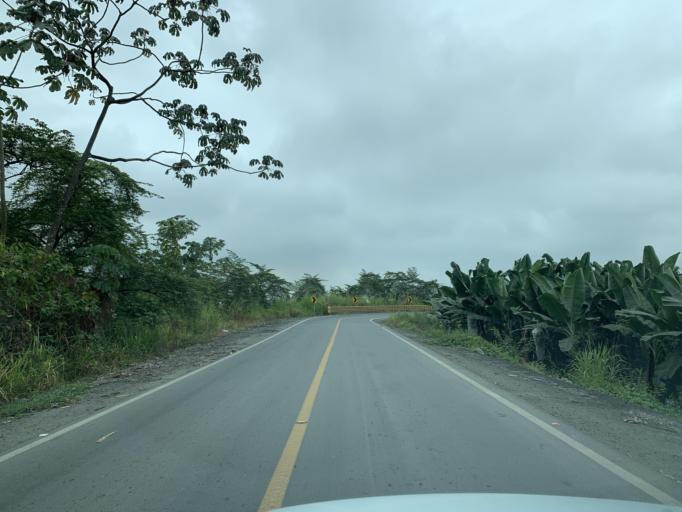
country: EC
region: Guayas
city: Coronel Marcelino Mariduena
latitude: -2.3004
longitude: -79.5034
